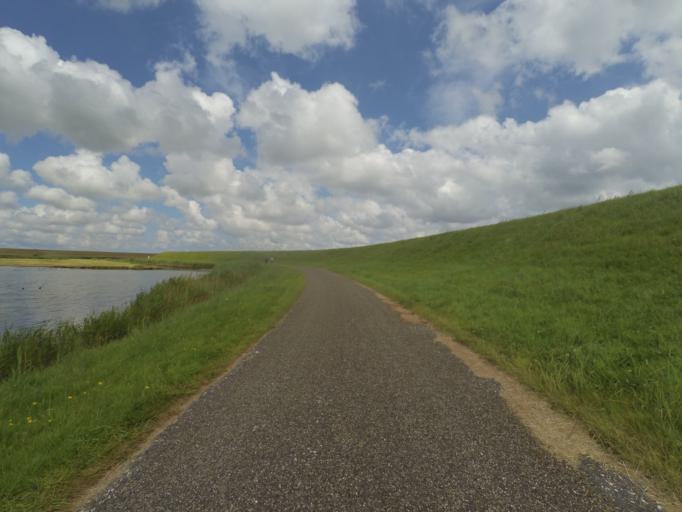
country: NL
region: North Holland
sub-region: Gemeente Texel
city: Den Burg
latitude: 53.0670
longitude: 4.8785
